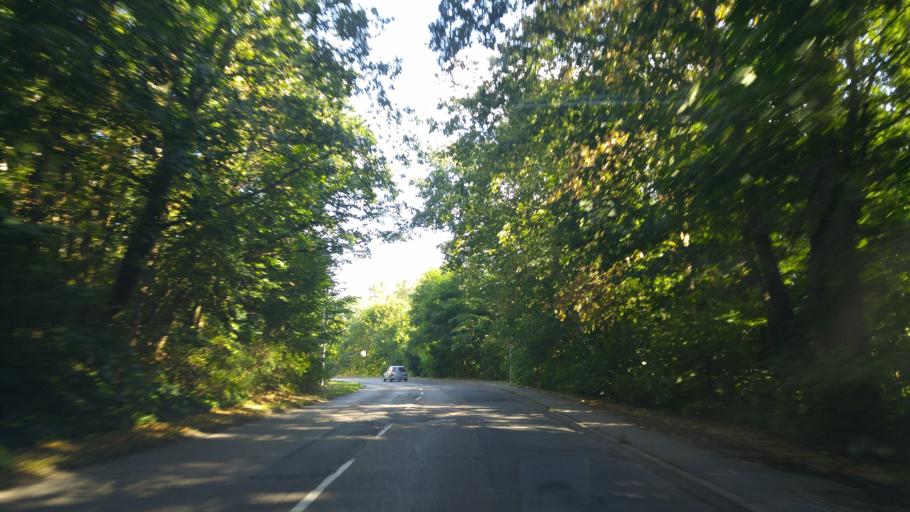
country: DE
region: Saxony-Anhalt
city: Lieskau
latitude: 51.5041
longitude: 11.8851
